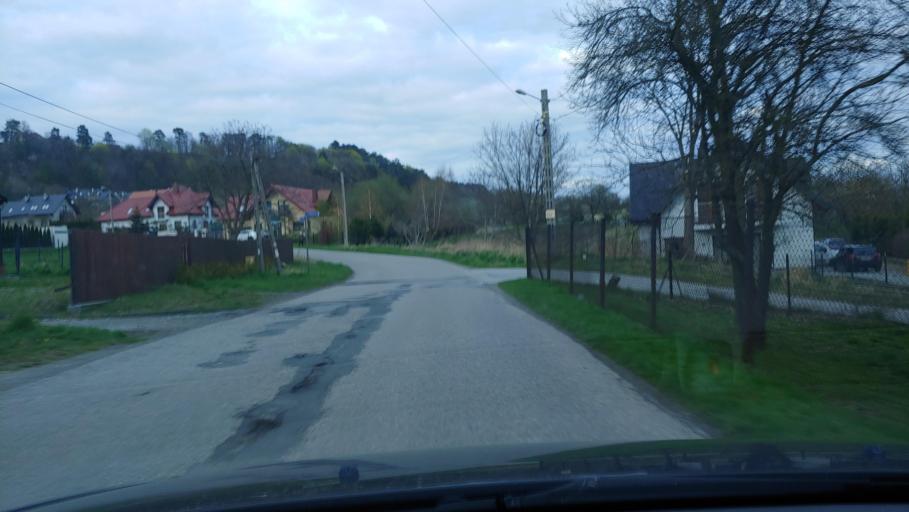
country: PL
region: Lesser Poland Voivodeship
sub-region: Powiat krakowski
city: Bolechowice
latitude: 50.1510
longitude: 19.7660
